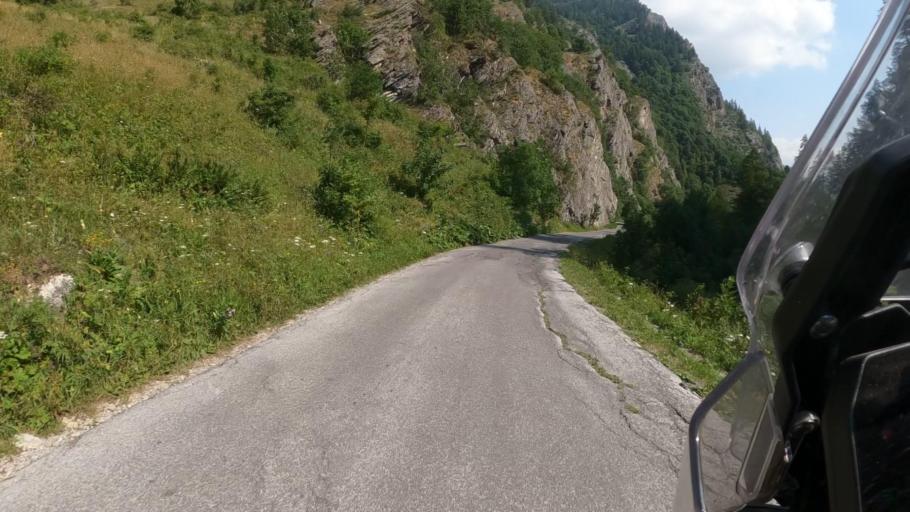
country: IT
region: Piedmont
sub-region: Provincia di Cuneo
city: Canosio
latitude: 44.4401
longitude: 7.0592
